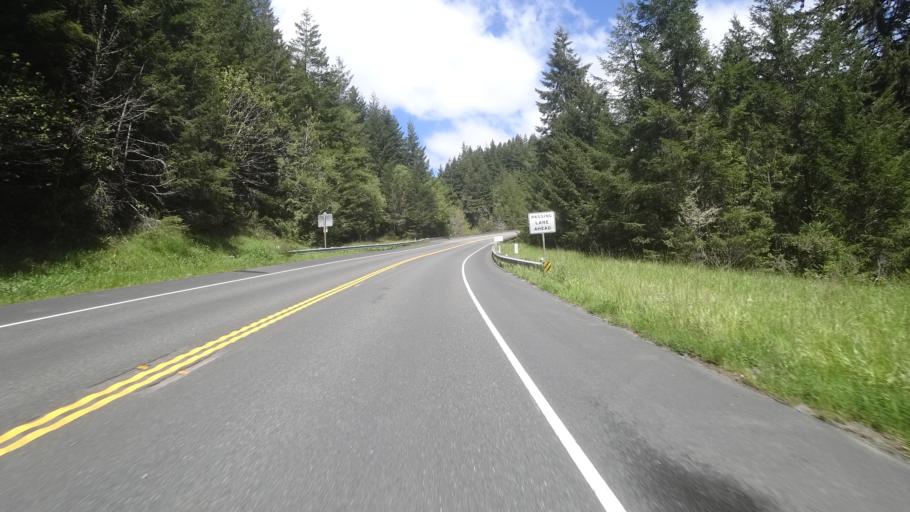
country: US
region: California
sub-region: Humboldt County
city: Blue Lake
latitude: 40.9127
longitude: -123.9164
